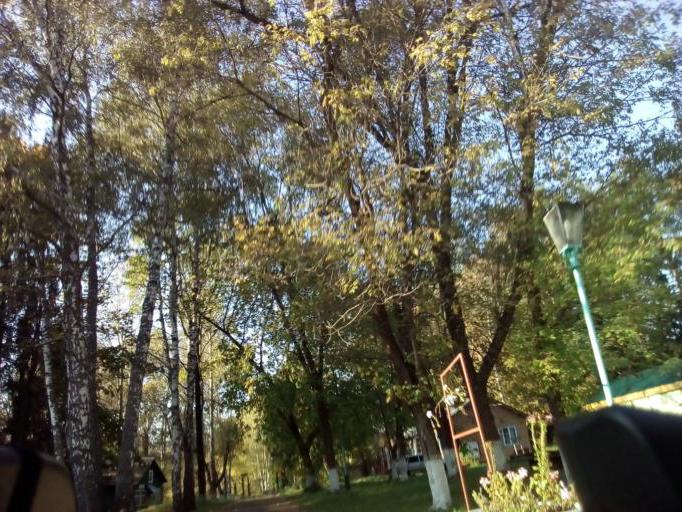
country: RU
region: Moskovskaya
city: Gzhel'
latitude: 55.5944
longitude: 38.3220
